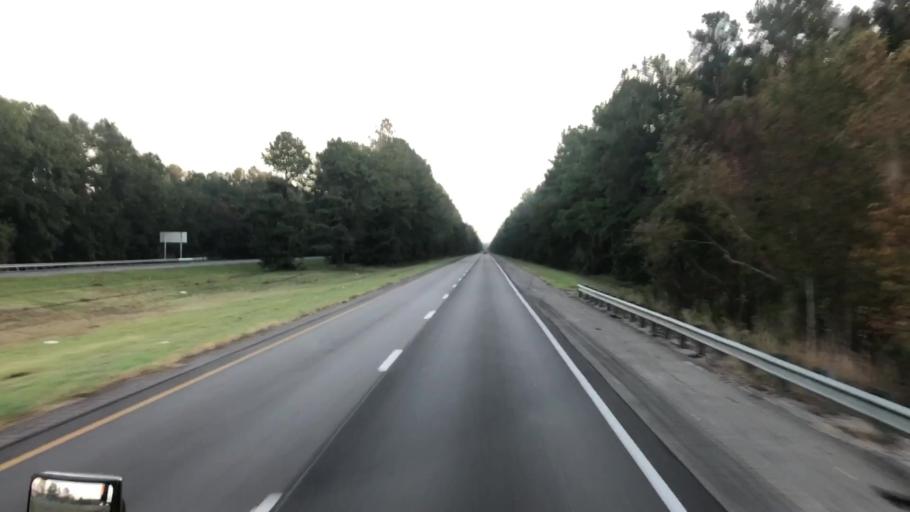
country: US
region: South Carolina
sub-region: Orangeburg County
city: Holly Hill
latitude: 33.5332
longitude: -80.4209
